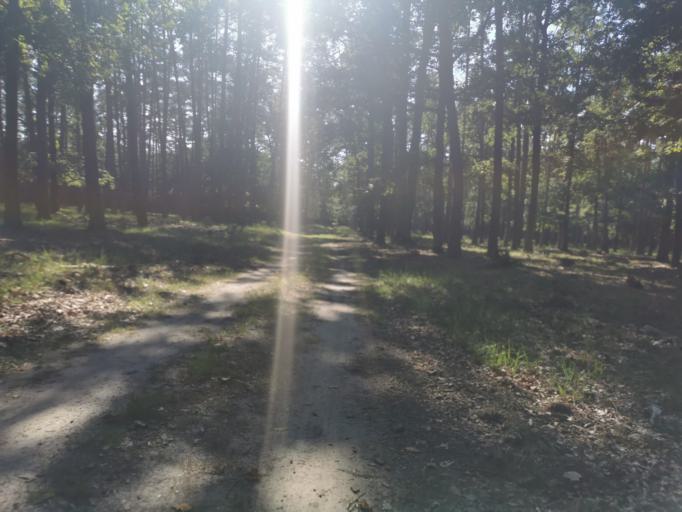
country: SK
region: Trnavsky
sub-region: Okres Senica
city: Senica
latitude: 48.6068
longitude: 17.2702
